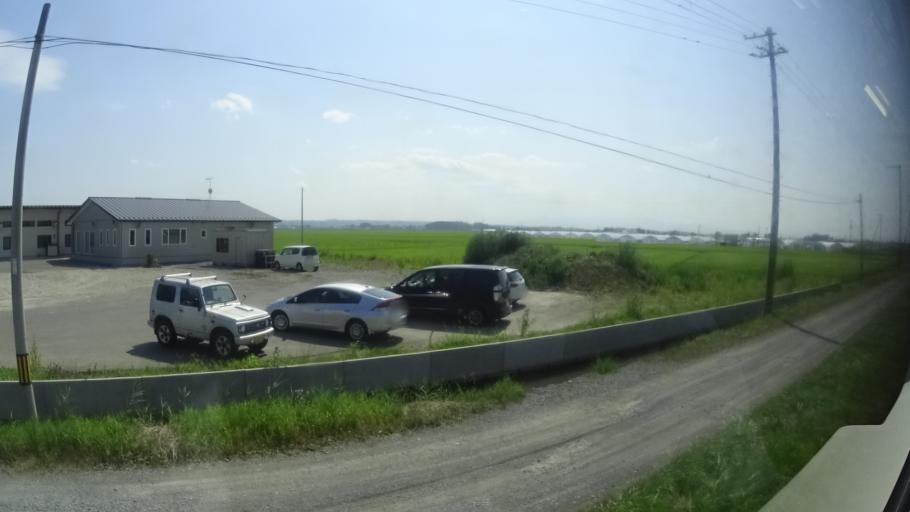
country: JP
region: Miyagi
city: Wakuya
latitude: 38.5499
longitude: 141.0974
